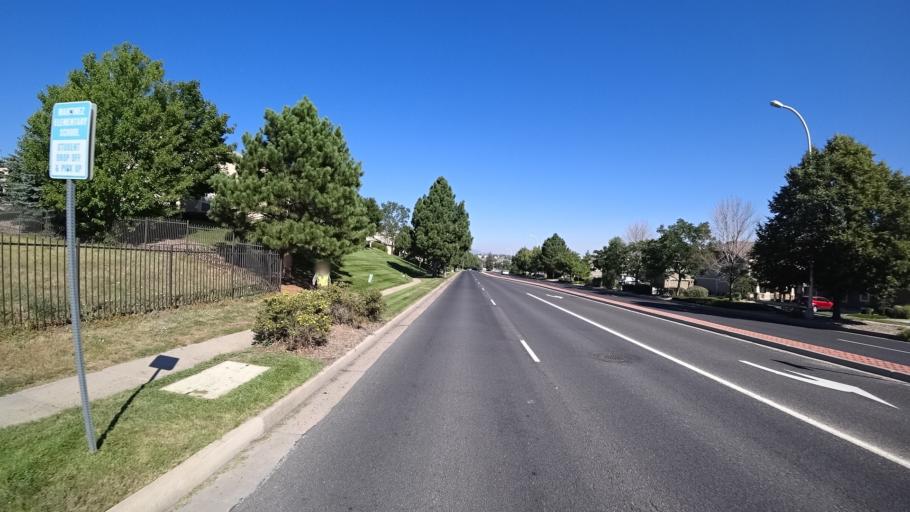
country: US
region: Colorado
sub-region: El Paso County
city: Cimarron Hills
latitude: 38.9248
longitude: -104.7500
